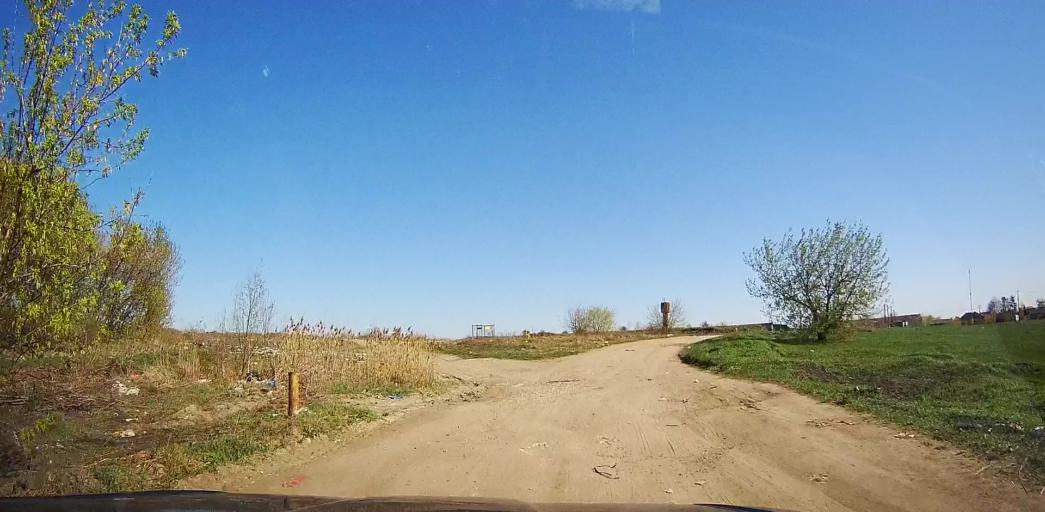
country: RU
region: Moskovskaya
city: Ramenskoye
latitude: 55.5562
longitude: 38.2853
